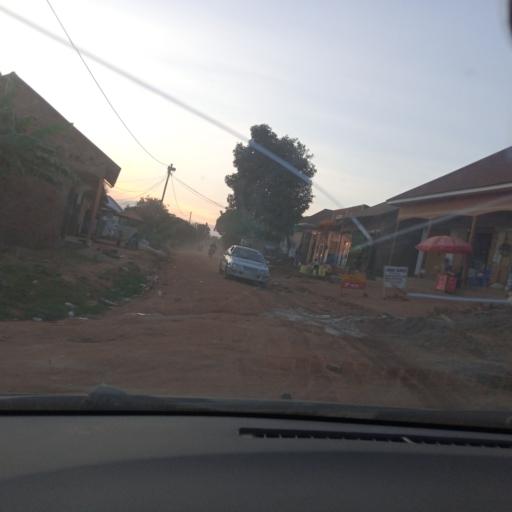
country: UG
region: Central Region
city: Masaka
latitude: -0.3134
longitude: 31.7676
